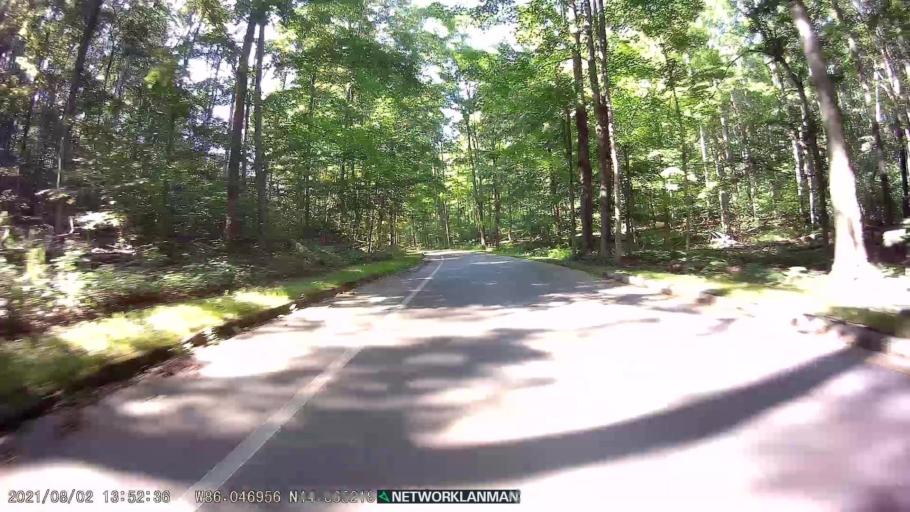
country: US
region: Michigan
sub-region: Benzie County
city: Beulah
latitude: 44.8651
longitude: -86.0469
